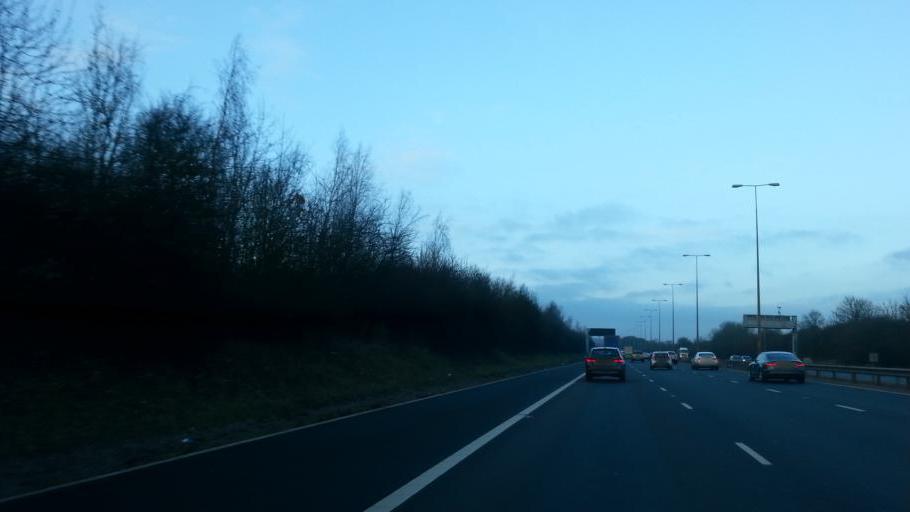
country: GB
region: England
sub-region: Worcestershire
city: Kempsey
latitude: 52.1446
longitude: -2.1944
